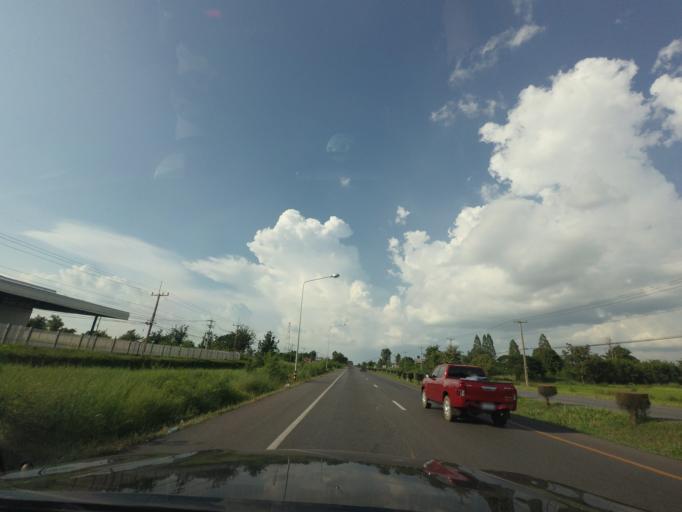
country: TH
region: Khon Kaen
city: Ban Haet
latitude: 16.1681
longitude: 102.7547
